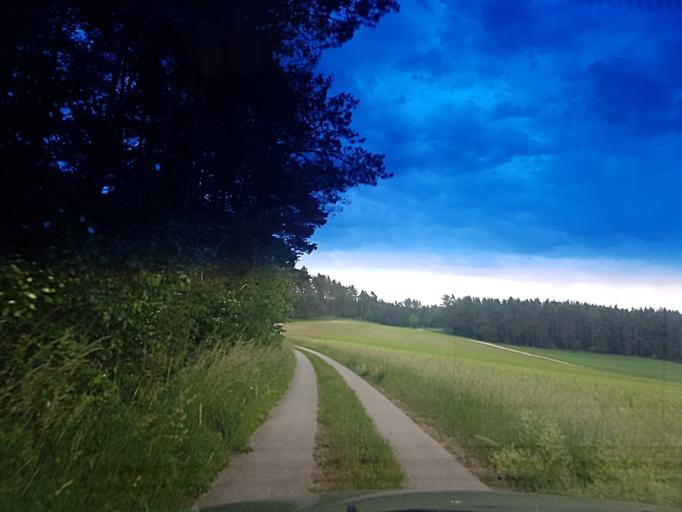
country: DE
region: Bavaria
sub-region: Upper Franconia
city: Wattendorf
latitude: 50.0106
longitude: 11.1218
